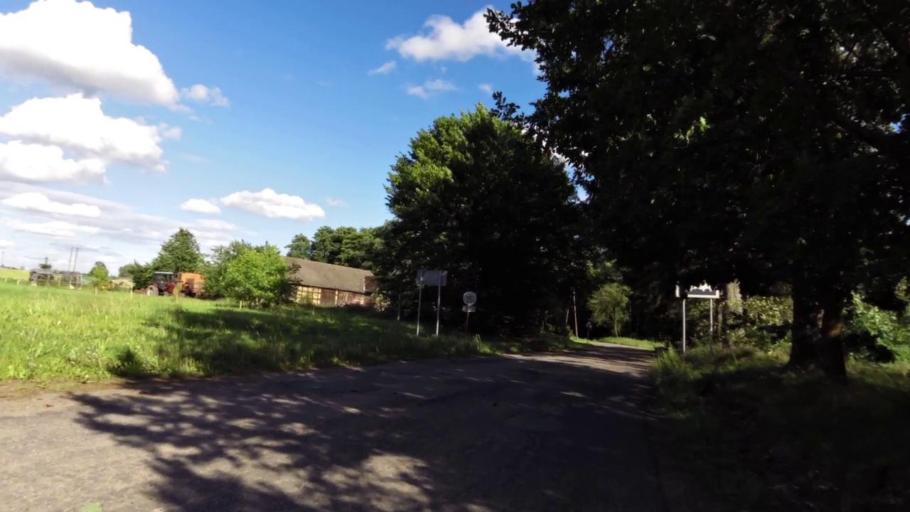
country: PL
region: West Pomeranian Voivodeship
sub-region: Powiat slawienski
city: Slawno
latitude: 54.4359
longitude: 16.7656
